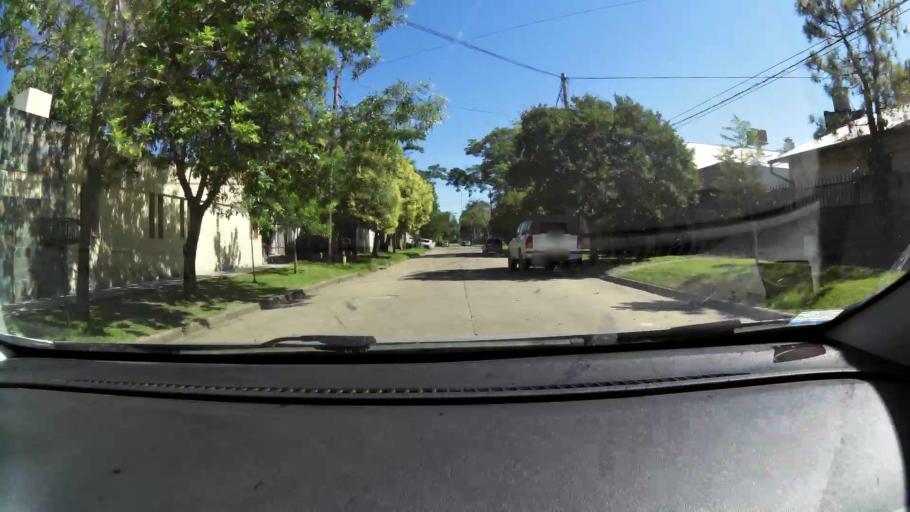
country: AR
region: Santa Fe
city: Santa Fe de la Vera Cruz
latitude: -31.6011
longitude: -60.6715
